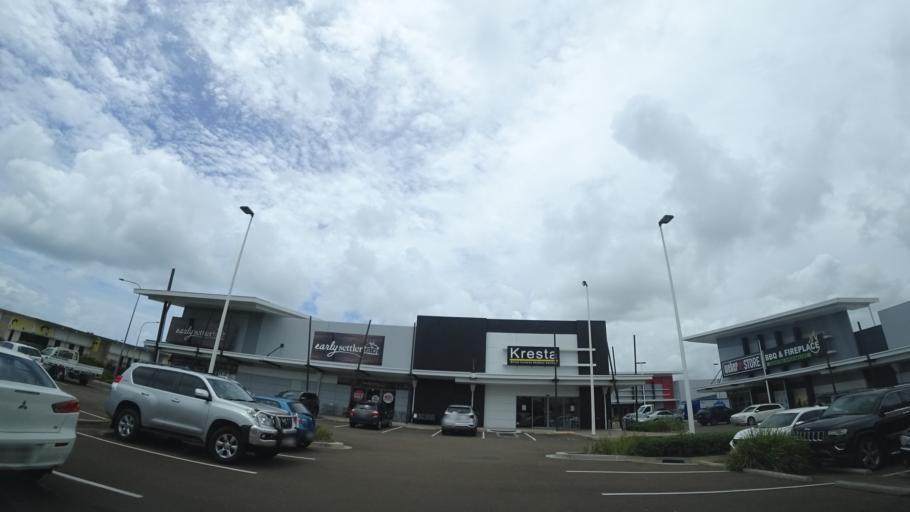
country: AU
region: Queensland
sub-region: Sunshine Coast
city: Dicky Beach
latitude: -26.7345
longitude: 153.1201
